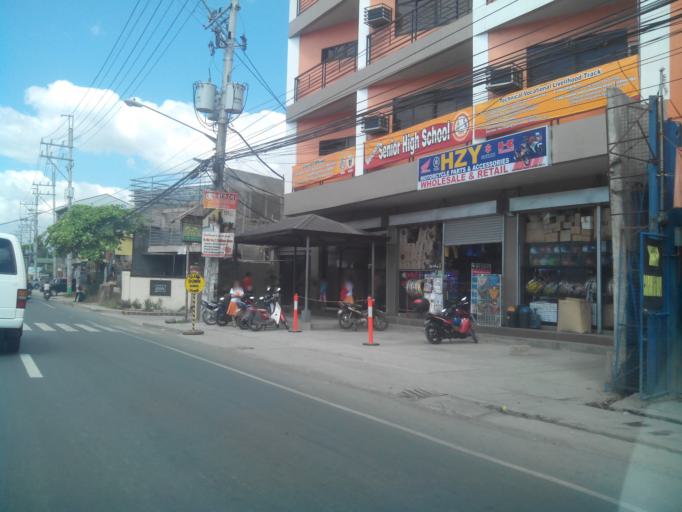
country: PH
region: Calabarzon
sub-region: Province of Rizal
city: Taytay
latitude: 14.5511
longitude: 121.1397
